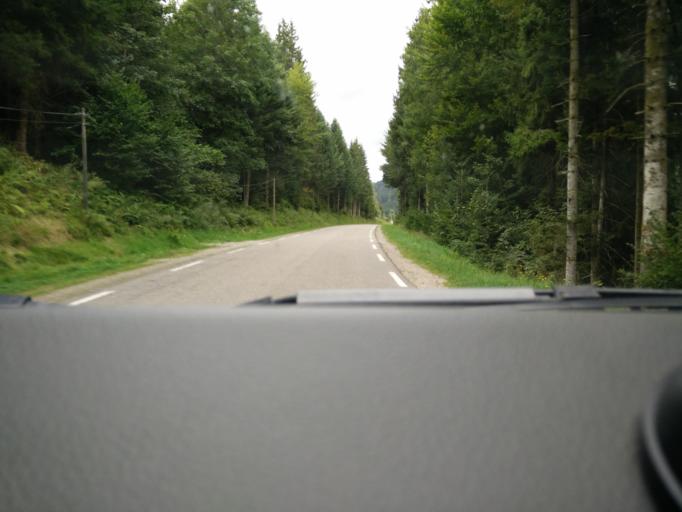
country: FR
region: Lorraine
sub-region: Departement des Vosges
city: Xonrupt-Longemer
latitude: 48.0793
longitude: 6.9374
